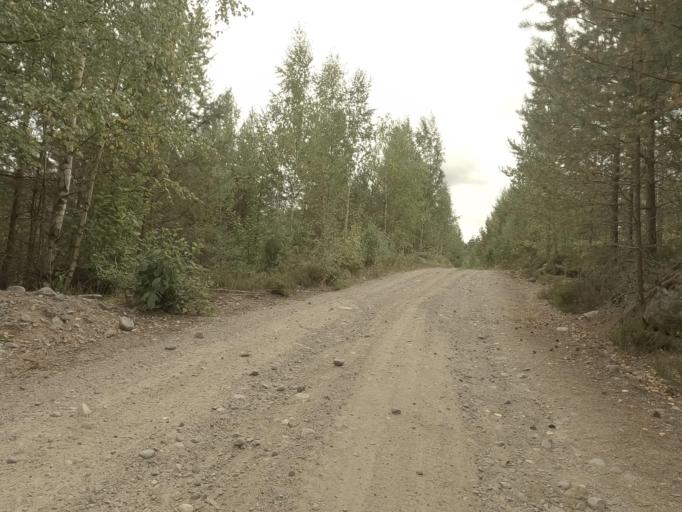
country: RU
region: Leningrad
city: Kamennogorsk
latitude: 61.0042
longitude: 29.1829
